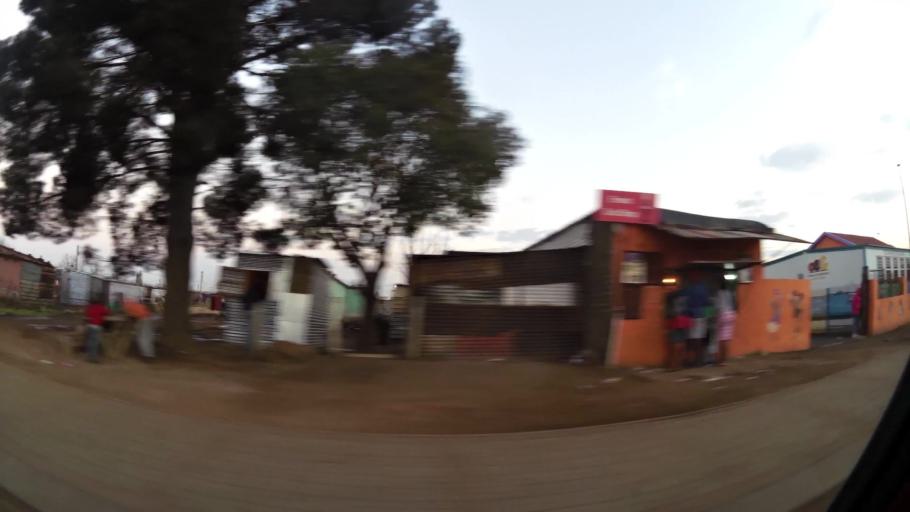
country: ZA
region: Gauteng
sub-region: City of Johannesburg Metropolitan Municipality
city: Orange Farm
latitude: -26.5464
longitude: 27.8401
